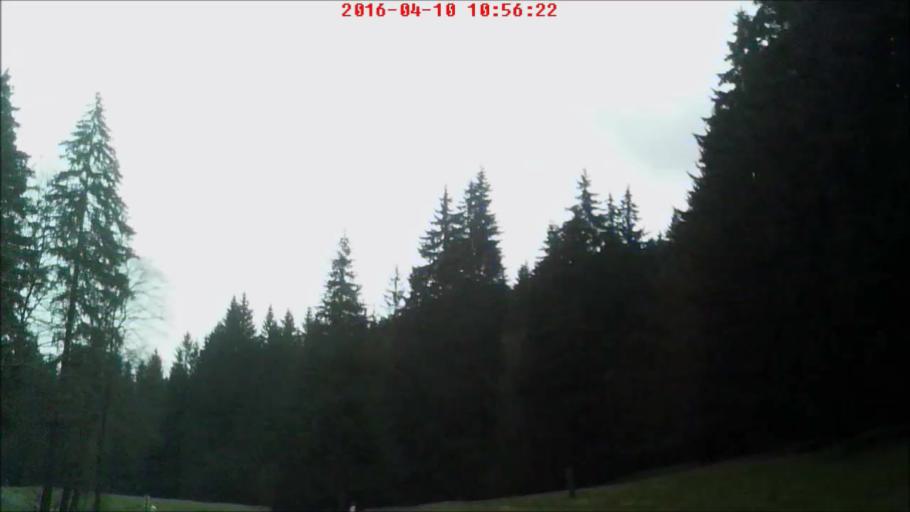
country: DE
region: Thuringia
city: Stutzerbach
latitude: 50.6218
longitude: 10.8554
